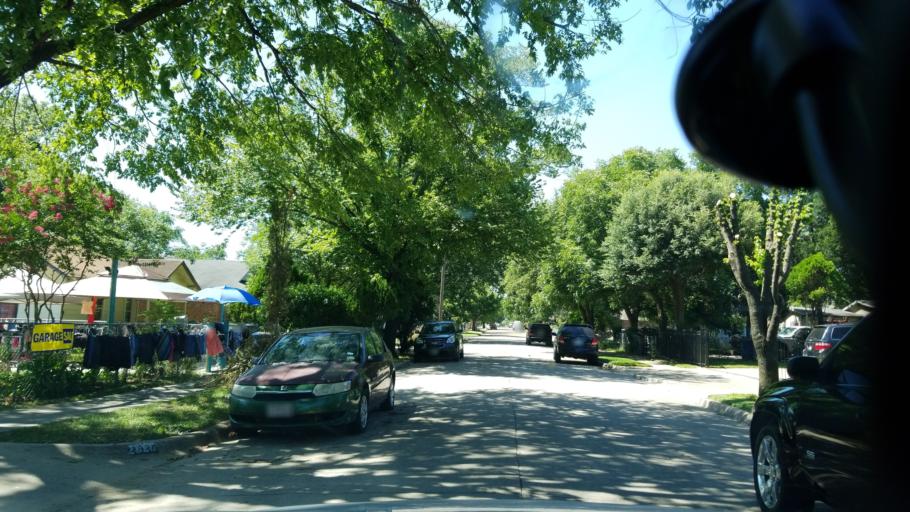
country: US
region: Texas
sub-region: Dallas County
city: Cockrell Hill
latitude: 32.7122
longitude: -96.8206
